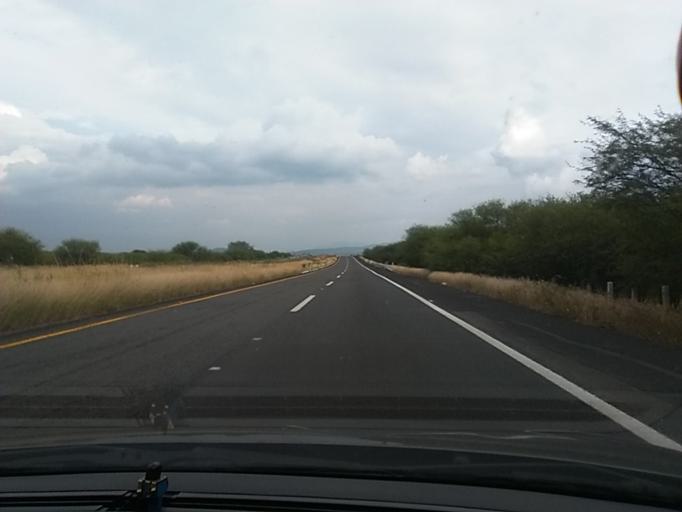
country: MX
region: Michoacan
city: Ecuandureo
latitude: 20.1797
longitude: -102.2699
